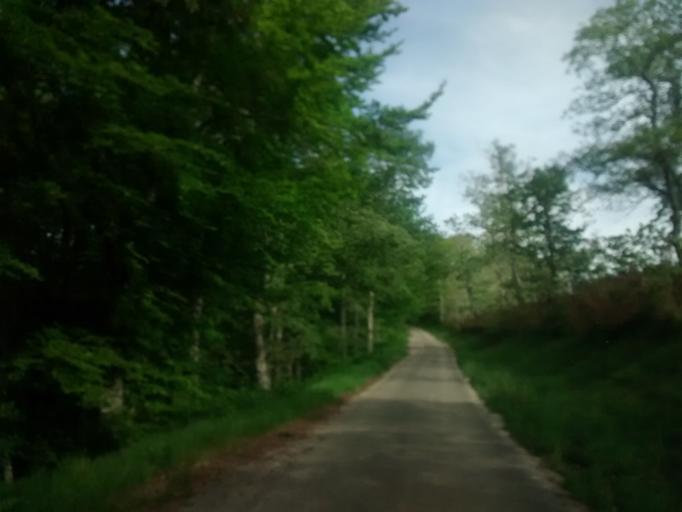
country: ES
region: Cantabria
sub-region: Provincia de Cantabria
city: Tresviso
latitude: 43.2428
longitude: -4.5745
